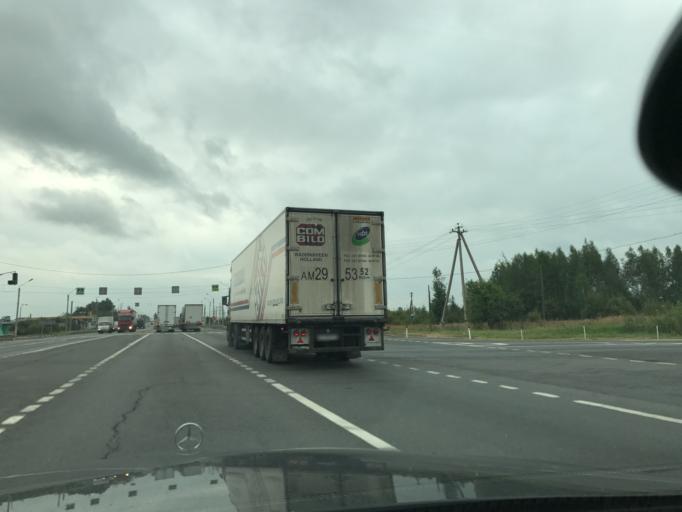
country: RU
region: Vladimir
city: Novovyazniki
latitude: 56.2194
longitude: 42.1836
